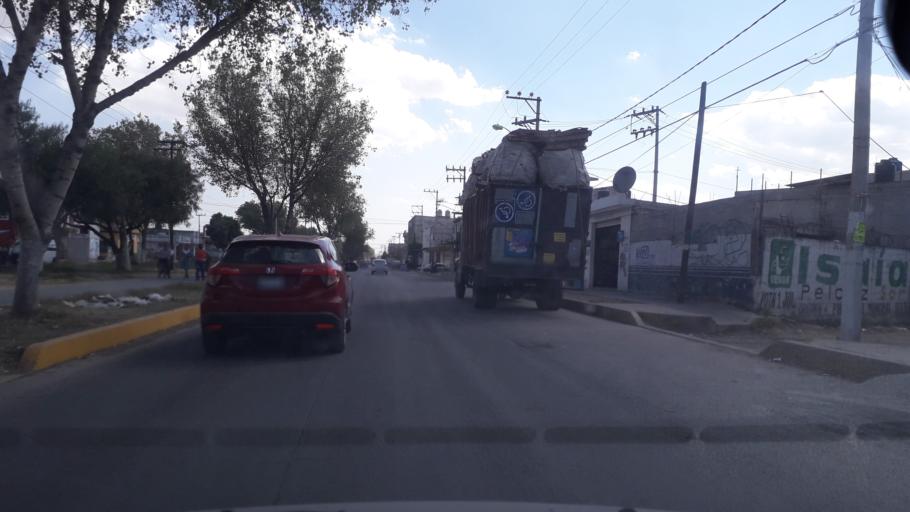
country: MX
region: Mexico
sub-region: Jaltenco
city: Alborada Jaltenco
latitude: 19.6471
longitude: -99.0624
